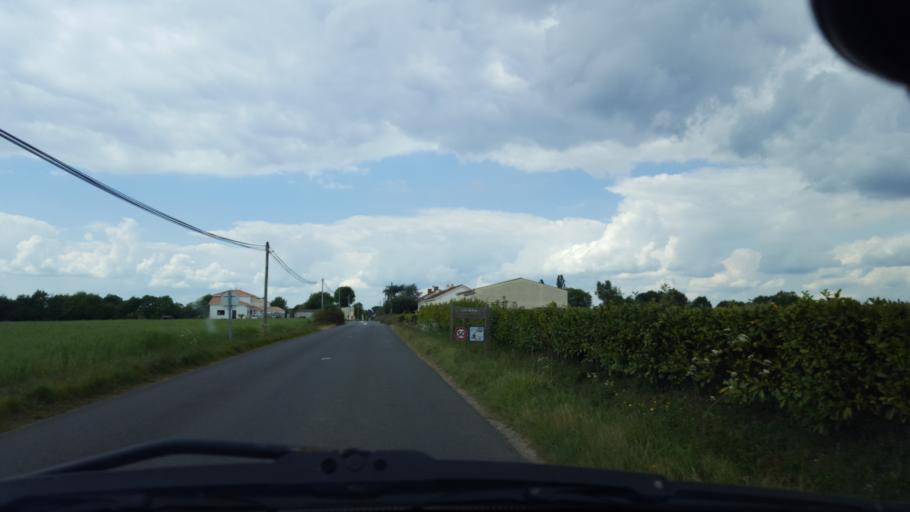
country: FR
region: Pays de la Loire
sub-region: Departement de la Loire-Atlantique
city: Saint-Philbert-de-Grand-Lieu
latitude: 47.0451
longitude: -1.6182
